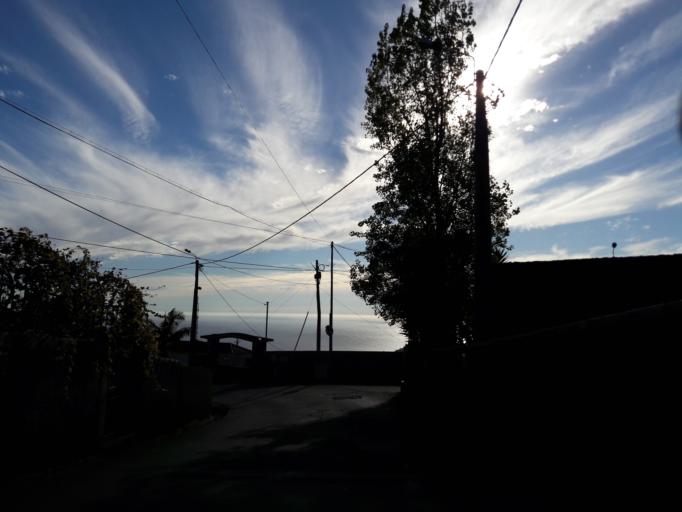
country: PT
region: Madeira
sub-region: Funchal
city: Nossa Senhora do Monte
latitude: 32.6742
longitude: -16.9110
